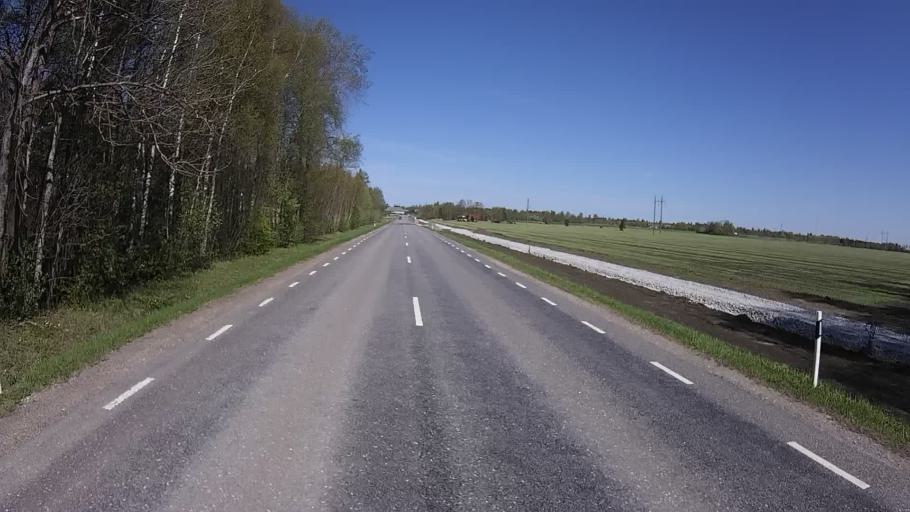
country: EE
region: Paernumaa
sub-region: Tootsi vald
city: Tootsi
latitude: 58.4981
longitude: 24.8022
